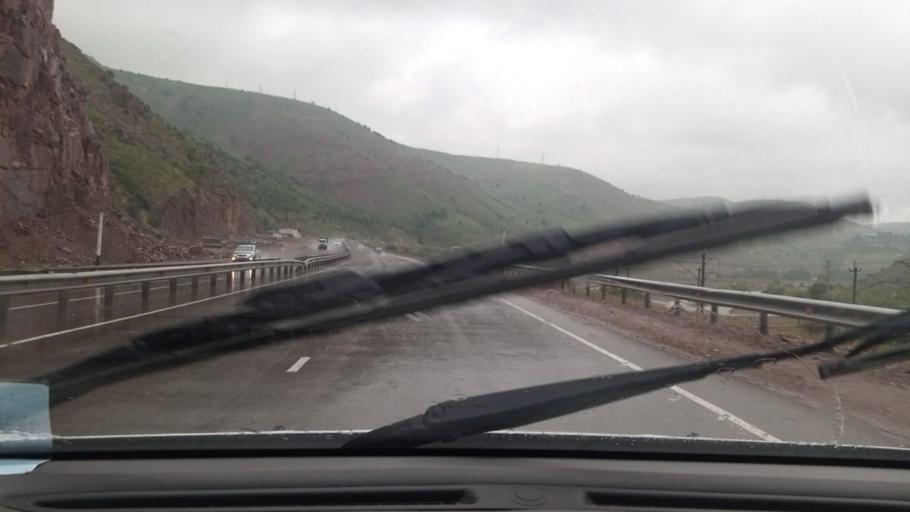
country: UZ
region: Toshkent
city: Angren
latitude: 41.0862
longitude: 70.3234
